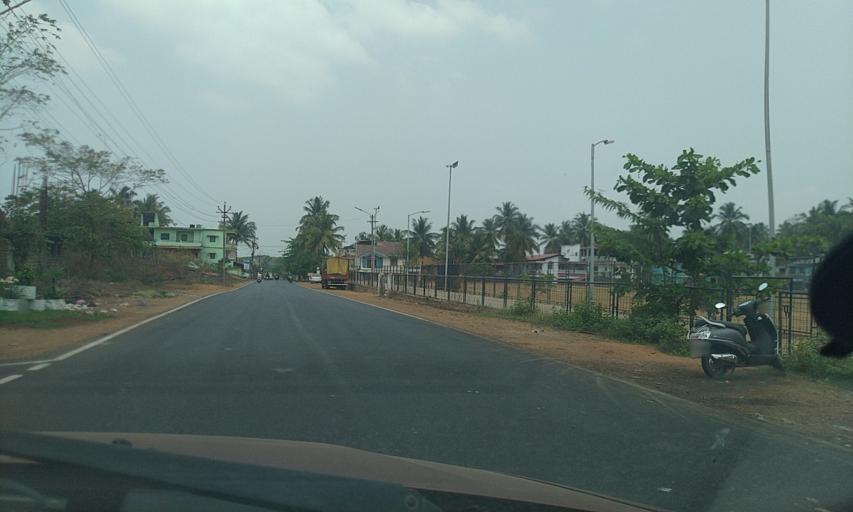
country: IN
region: Goa
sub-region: North Goa
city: Mapuca
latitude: 15.6056
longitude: 73.8040
